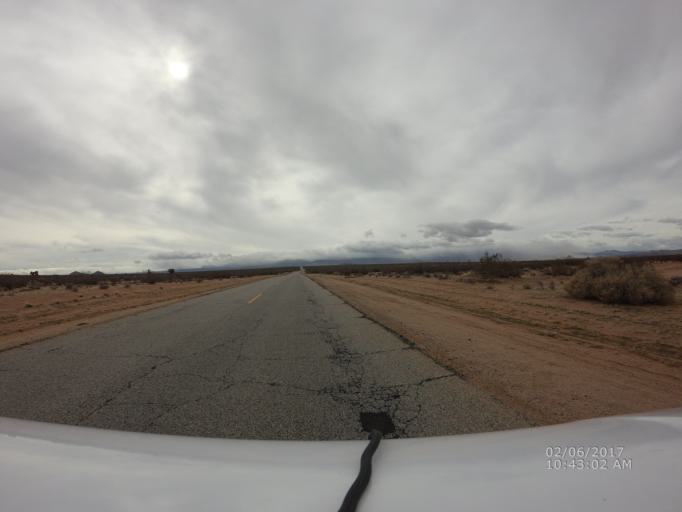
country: US
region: California
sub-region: Los Angeles County
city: Lake Los Angeles
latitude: 34.6567
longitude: -117.7023
